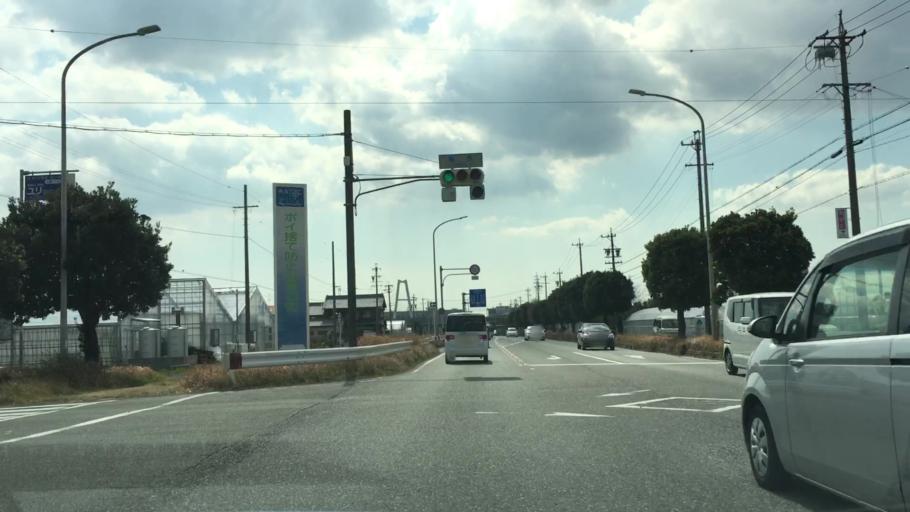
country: JP
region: Aichi
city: Kozakai-cho
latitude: 34.8118
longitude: 137.3109
